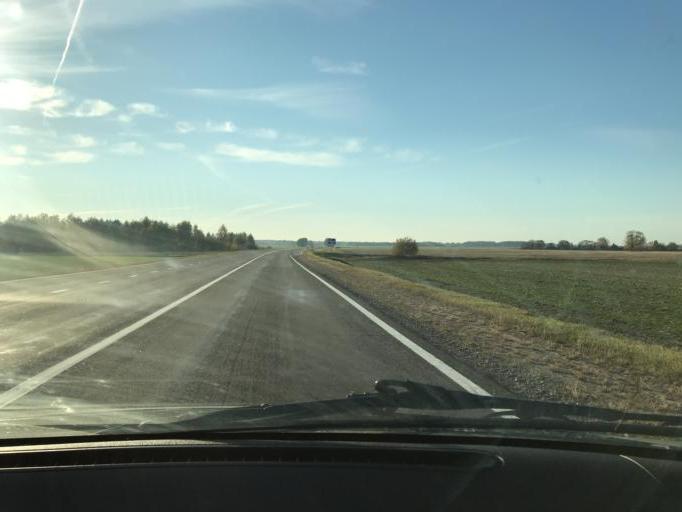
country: BY
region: Brest
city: Antopal'
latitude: 52.2073
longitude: 24.6060
